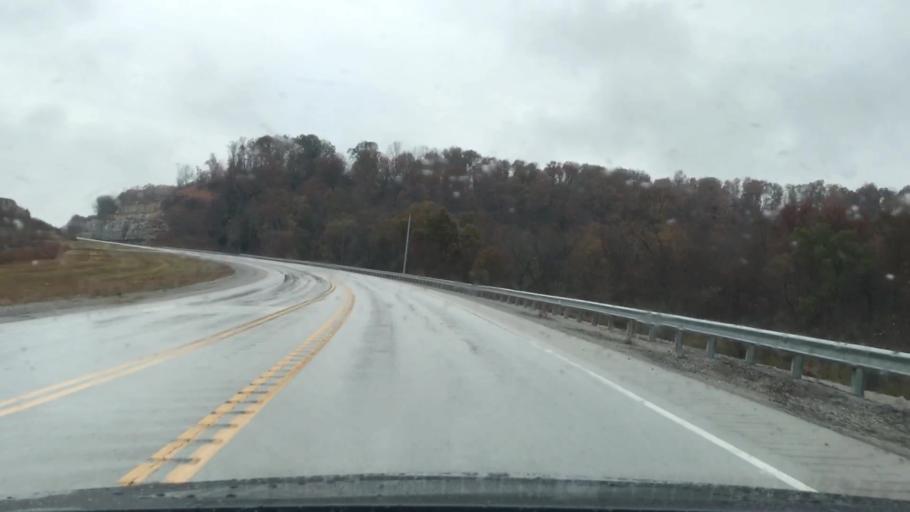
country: US
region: Kentucky
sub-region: Logan County
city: Russellville
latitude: 36.8315
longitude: -86.8611
